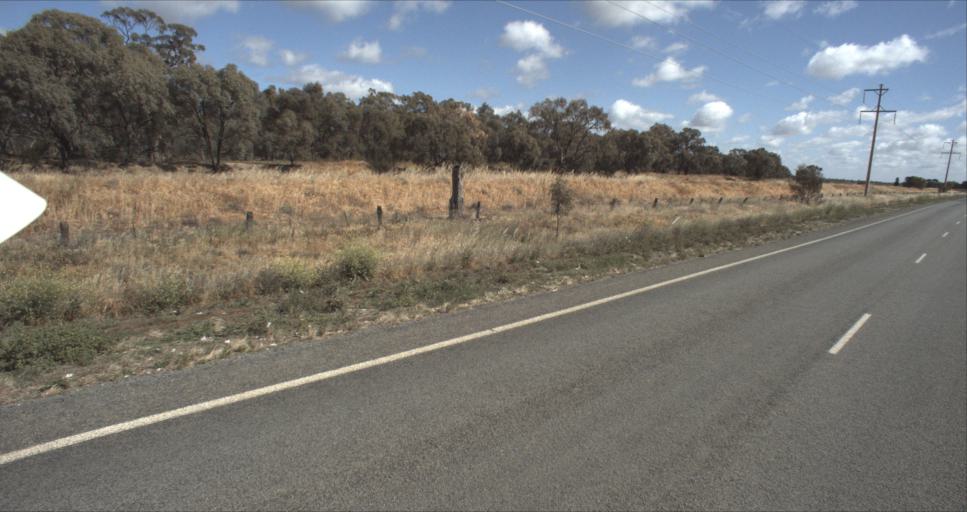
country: AU
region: New South Wales
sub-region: Murrumbidgee Shire
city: Darlington Point
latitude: -34.5450
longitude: 146.1715
